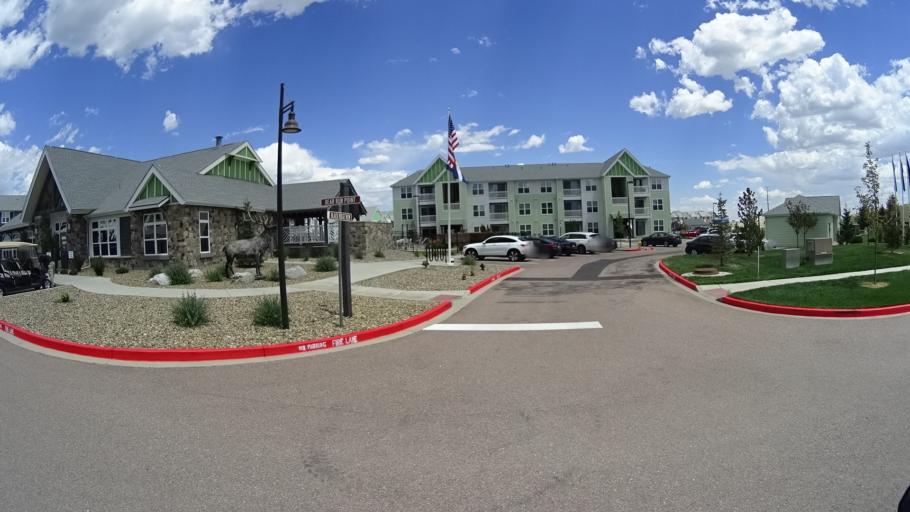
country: US
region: Colorado
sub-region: El Paso County
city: Black Forest
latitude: 38.9430
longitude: -104.7113
